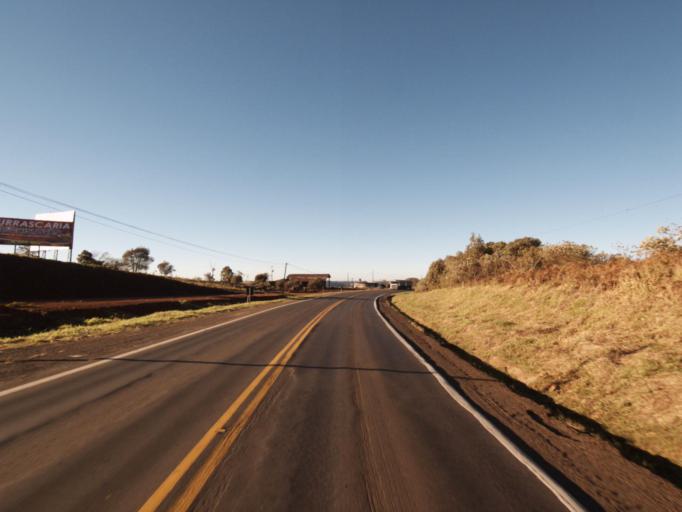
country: AR
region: Misiones
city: Bernardo de Irigoyen
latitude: -26.3071
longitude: -53.5474
